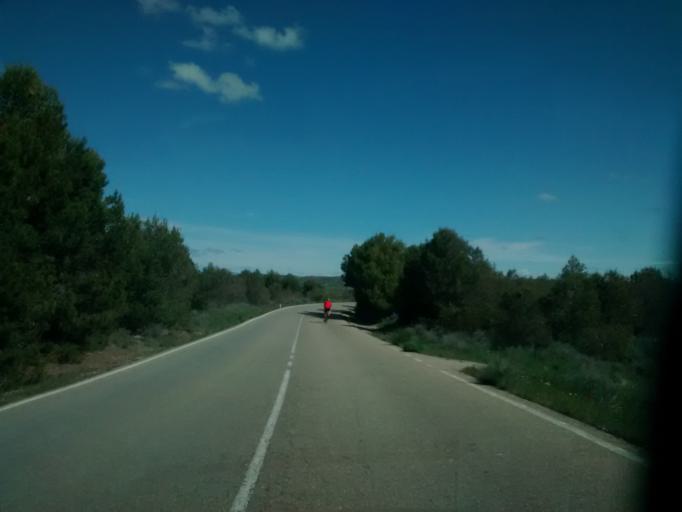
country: ES
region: Aragon
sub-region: Provincia de Zaragoza
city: Lecinena
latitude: 41.7909
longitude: -0.6201
